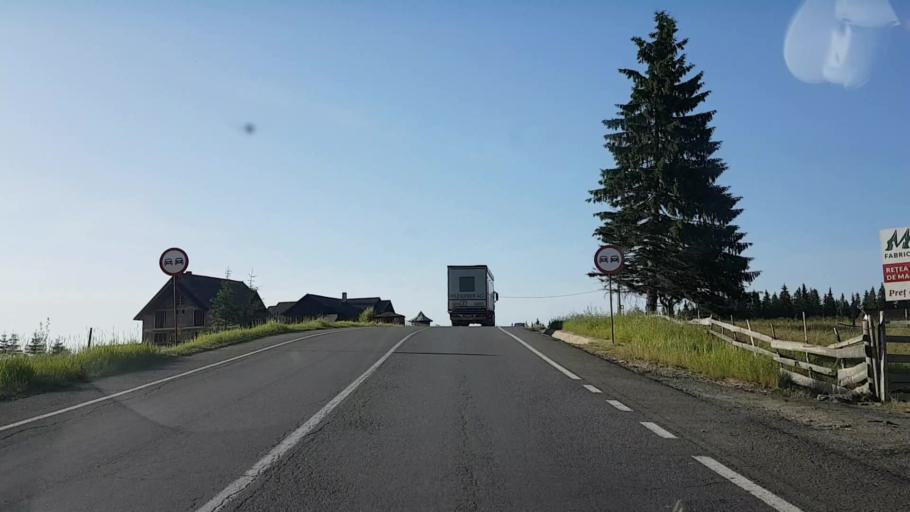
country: RO
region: Bistrita-Nasaud
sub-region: Comuna Lunca Ilvei
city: Lunca Ilvei
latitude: 47.2759
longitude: 25.0283
